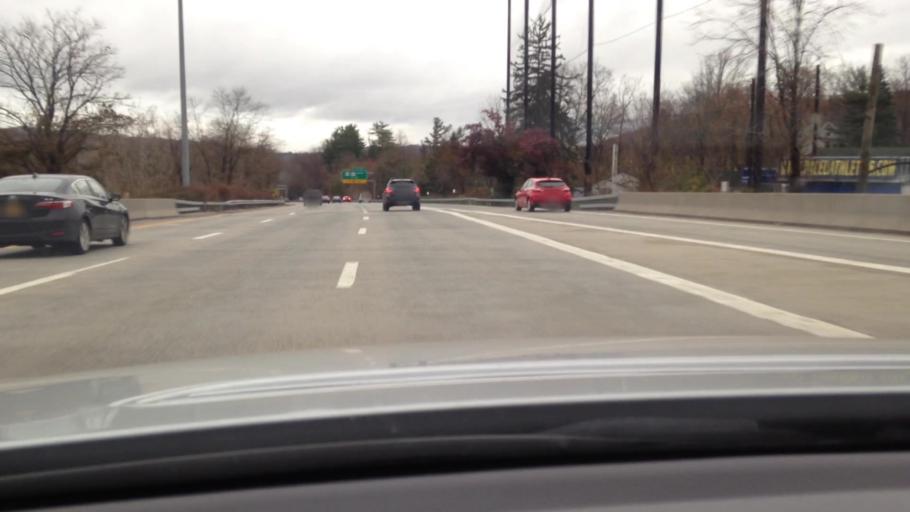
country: US
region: New York
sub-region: Westchester County
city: Pleasantville
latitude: 41.1237
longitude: -73.8087
